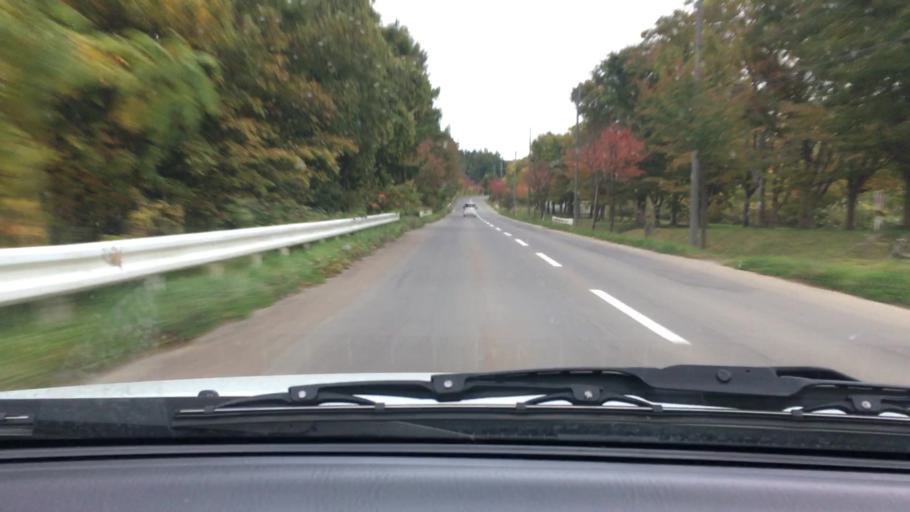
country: JP
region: Aomori
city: Shimokizukuri
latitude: 40.7173
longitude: 140.3054
